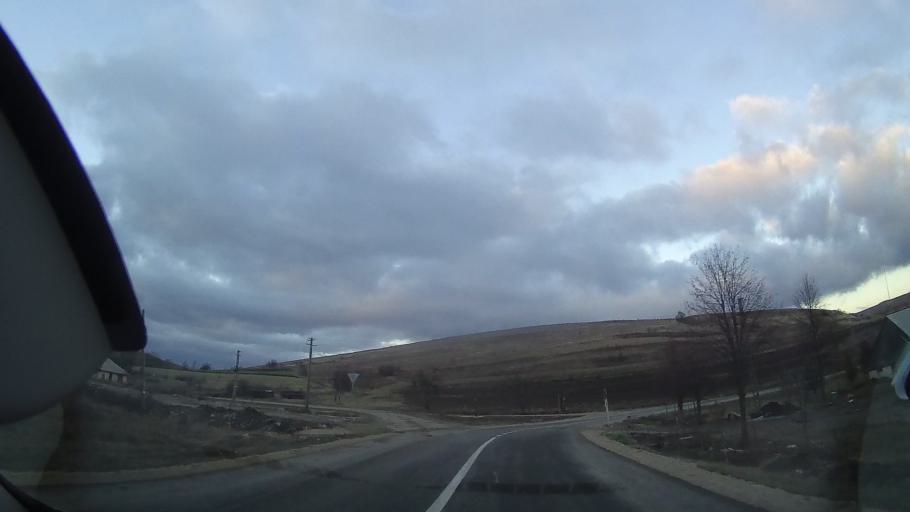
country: RO
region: Cluj
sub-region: Comuna Izvoru Crisului
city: Izvoru Crisului
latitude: 46.8034
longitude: 23.1093
